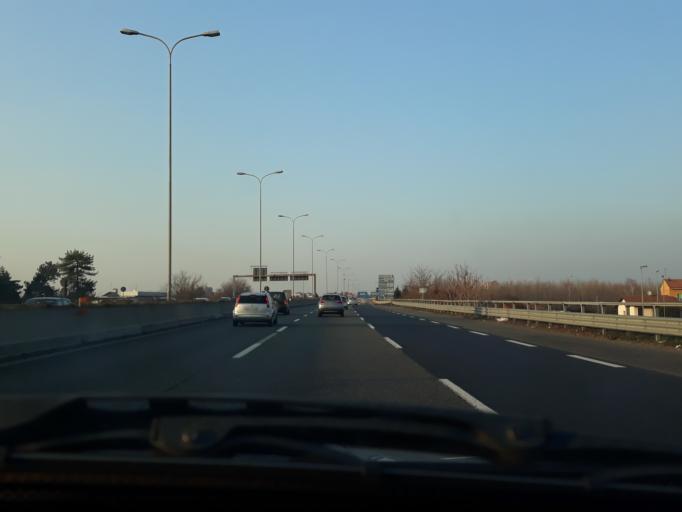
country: IT
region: Lombardy
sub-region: Provincia di Monza e Brianza
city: Muggio
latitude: 45.5900
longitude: 9.2469
